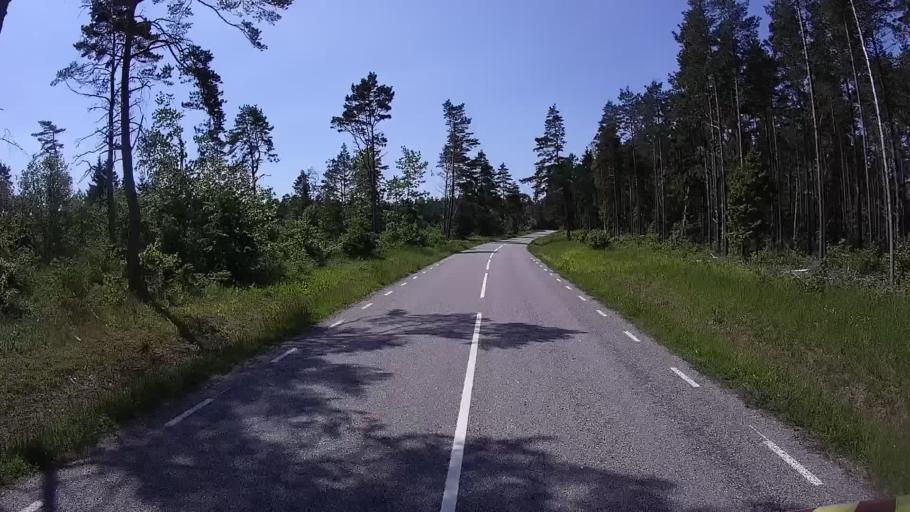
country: EE
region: Saare
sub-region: Kuressaare linn
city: Kuressaare
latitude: 57.9680
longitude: 22.1228
